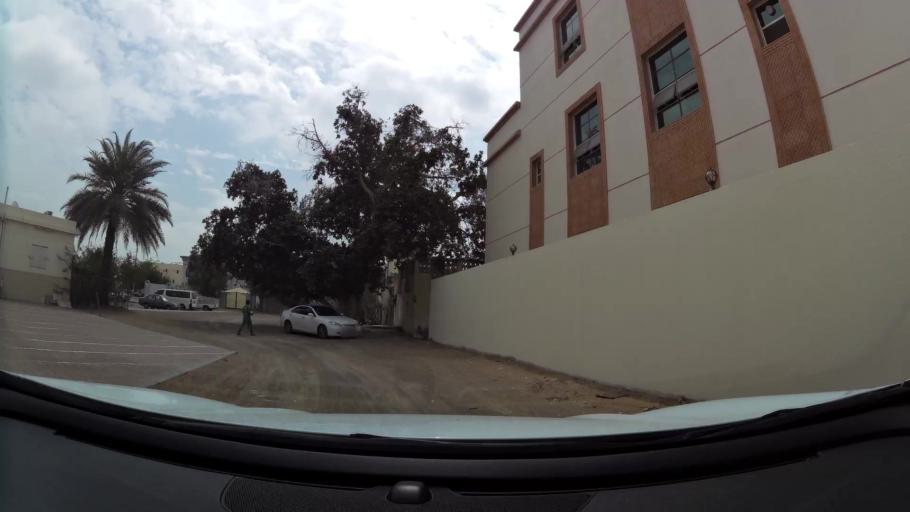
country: AE
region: Abu Dhabi
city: Al Ain
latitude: 24.2181
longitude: 55.7779
